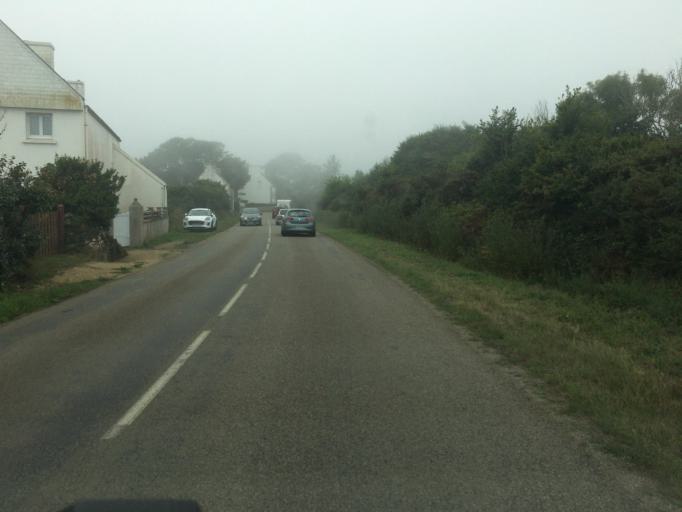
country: FR
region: Brittany
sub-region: Departement du Finistere
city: Plogoff
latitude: 48.0571
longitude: -4.6950
